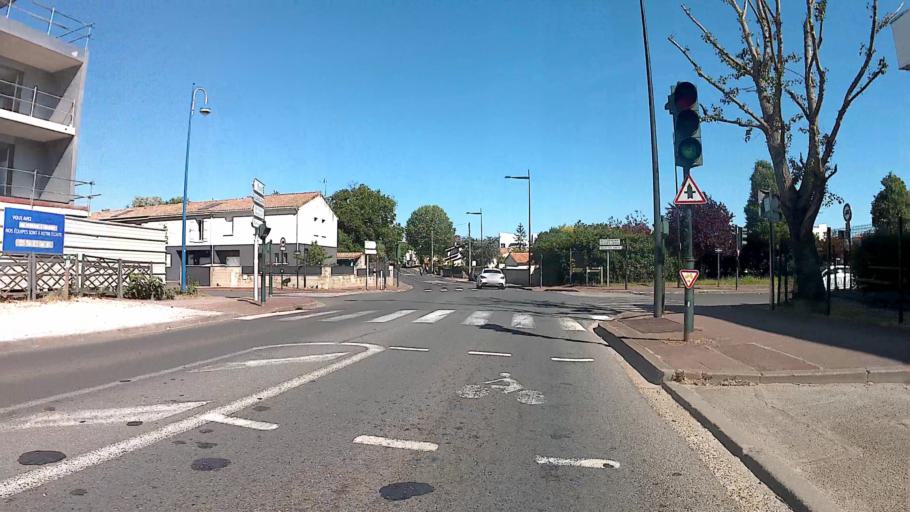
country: FR
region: Aquitaine
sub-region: Departement de la Gironde
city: Begles
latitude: 44.7976
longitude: -0.5412
